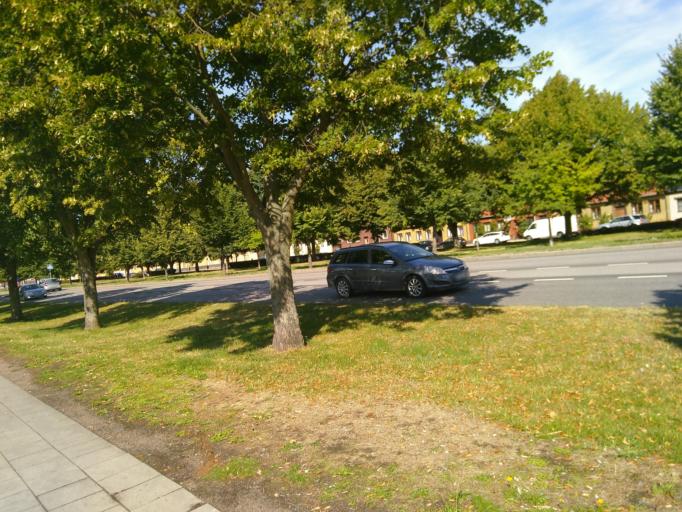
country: SE
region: Skane
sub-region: Landskrona
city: Landskrona
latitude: 55.8710
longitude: 12.8482
